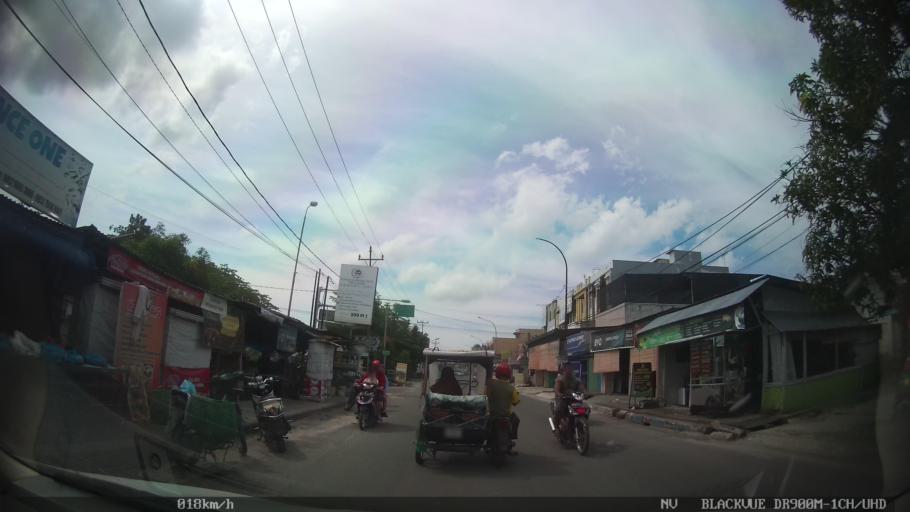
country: ID
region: North Sumatra
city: Percut
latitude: 3.5676
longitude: 98.8717
